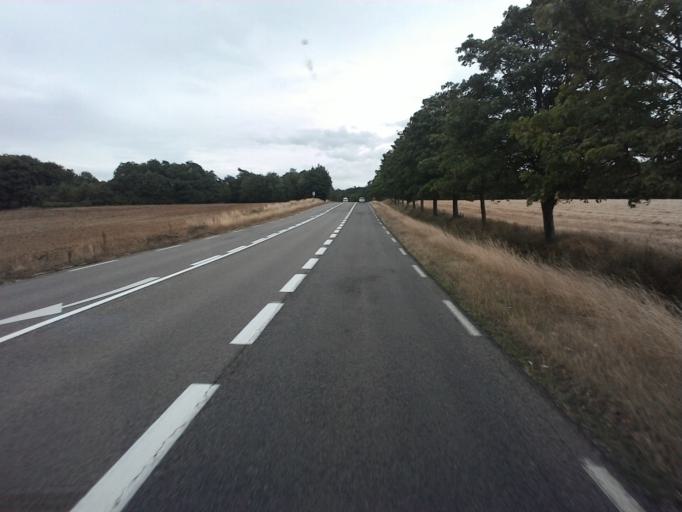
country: FR
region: Lorraine
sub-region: Departement de Meurthe-et-Moselle
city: Colombey-les-Belles
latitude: 48.5757
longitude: 5.9846
